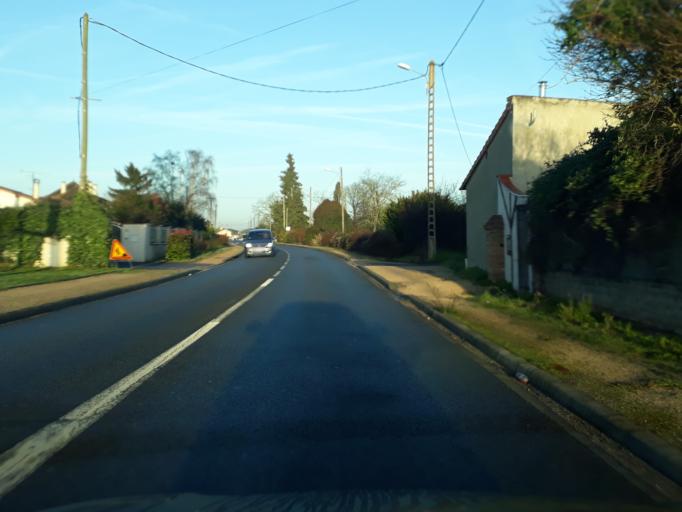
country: FR
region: Midi-Pyrenees
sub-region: Departement de la Haute-Garonne
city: Longages
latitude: 43.3563
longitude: 1.2344
